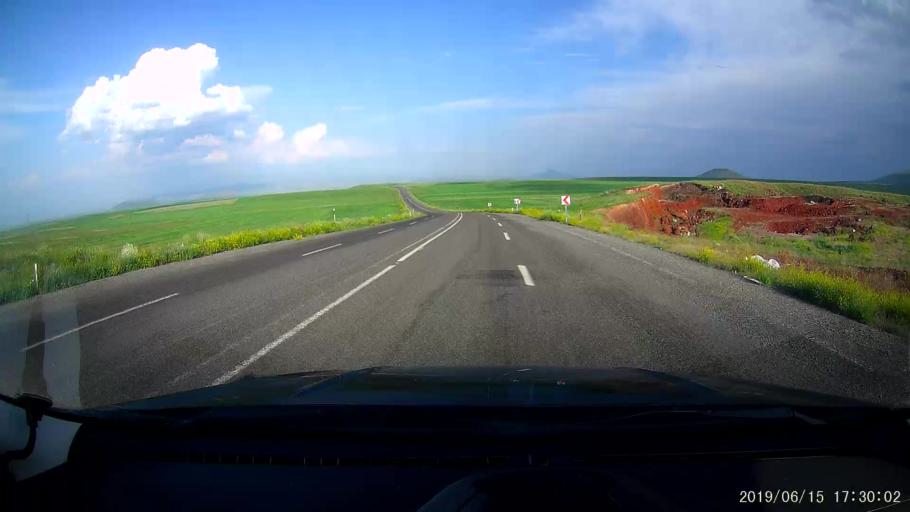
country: TR
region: Kars
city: Basgedikler
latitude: 40.5853
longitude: 43.4620
